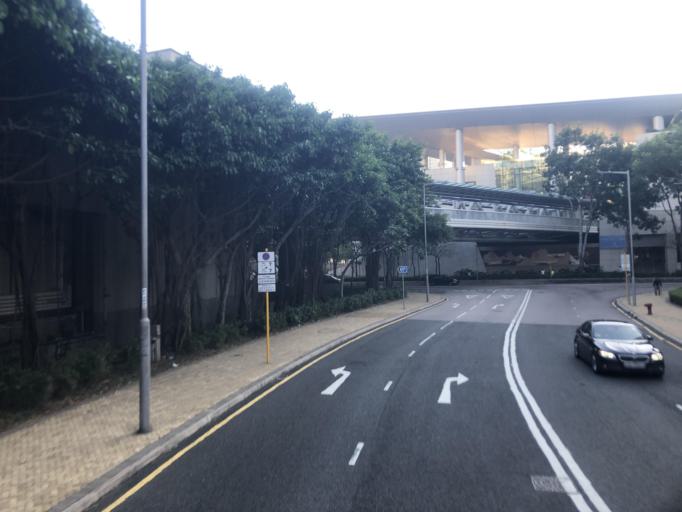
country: HK
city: Tai O
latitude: 22.2919
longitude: 113.9435
